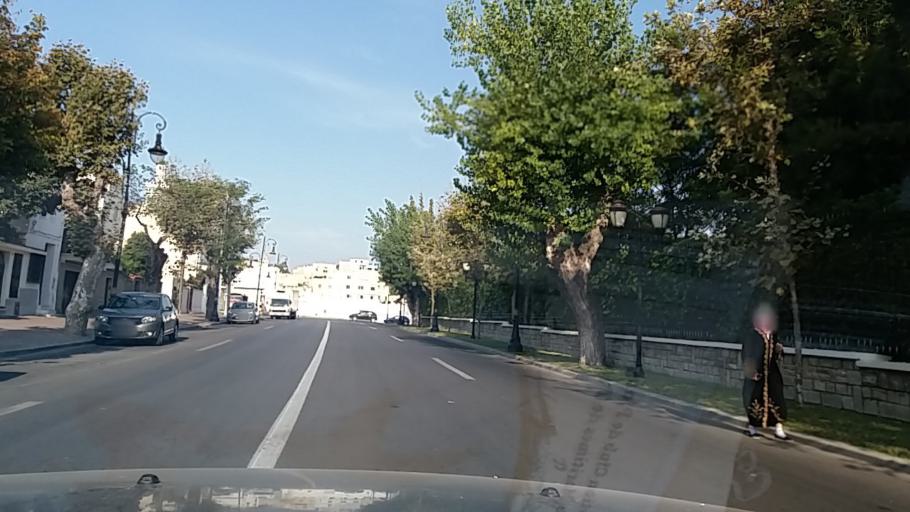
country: MA
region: Tanger-Tetouan
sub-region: Tanger-Assilah
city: Tangier
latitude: 35.7902
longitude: -5.8270
